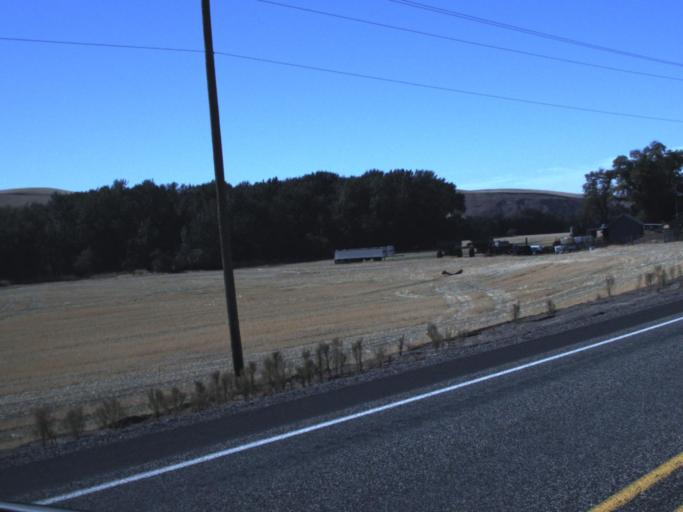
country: US
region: Washington
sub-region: Walla Walla County
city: Waitsburg
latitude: 46.2806
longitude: -118.2336
